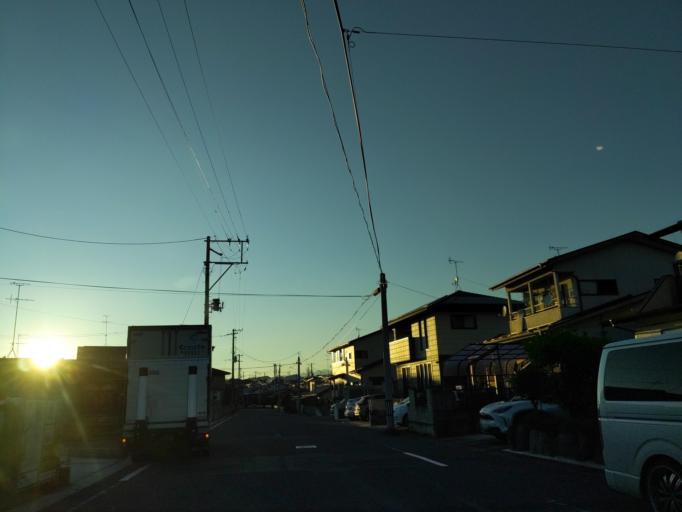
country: JP
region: Fukushima
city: Koriyama
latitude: 37.4092
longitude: 140.3342
